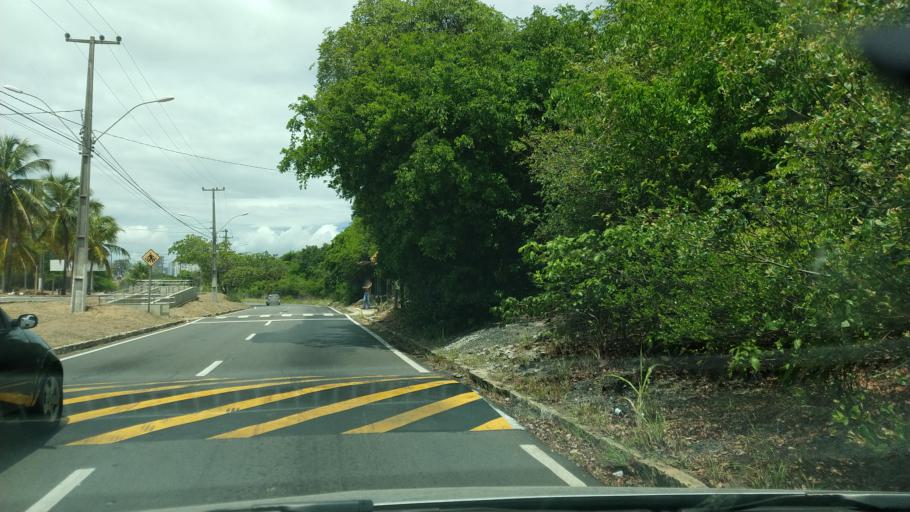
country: BR
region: Rio Grande do Norte
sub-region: Natal
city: Natal
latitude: -5.8376
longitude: -35.1969
